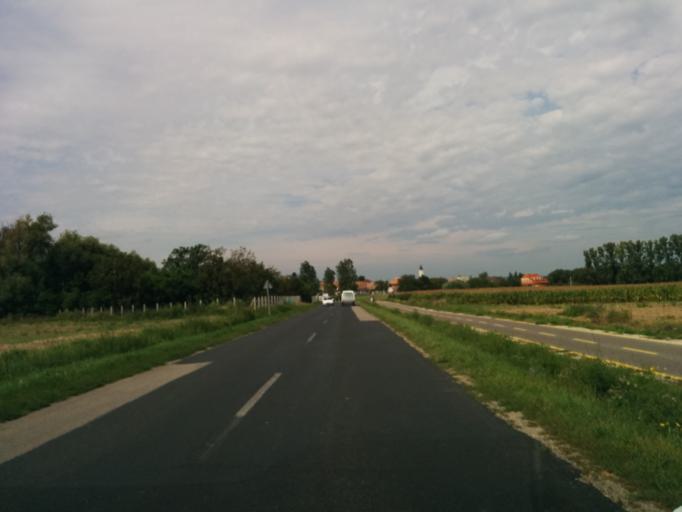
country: HU
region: Gyor-Moson-Sopron
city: Fertod
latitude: 47.6191
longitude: 16.8052
